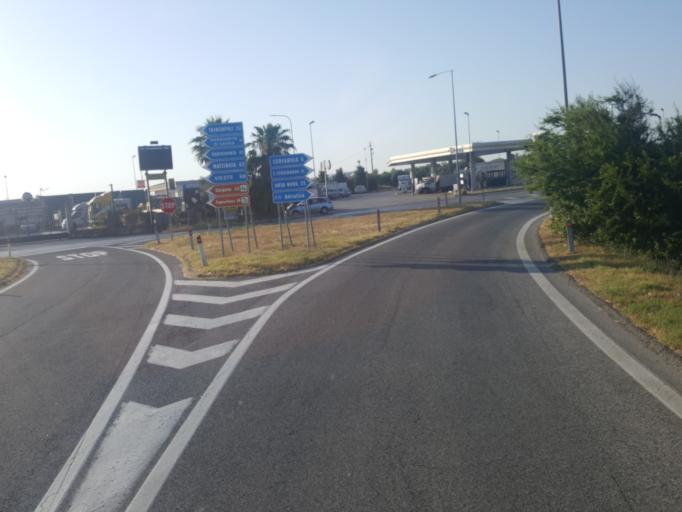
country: IT
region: Apulia
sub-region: Provincia di Foggia
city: Cerignola
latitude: 41.3199
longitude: 15.8996
